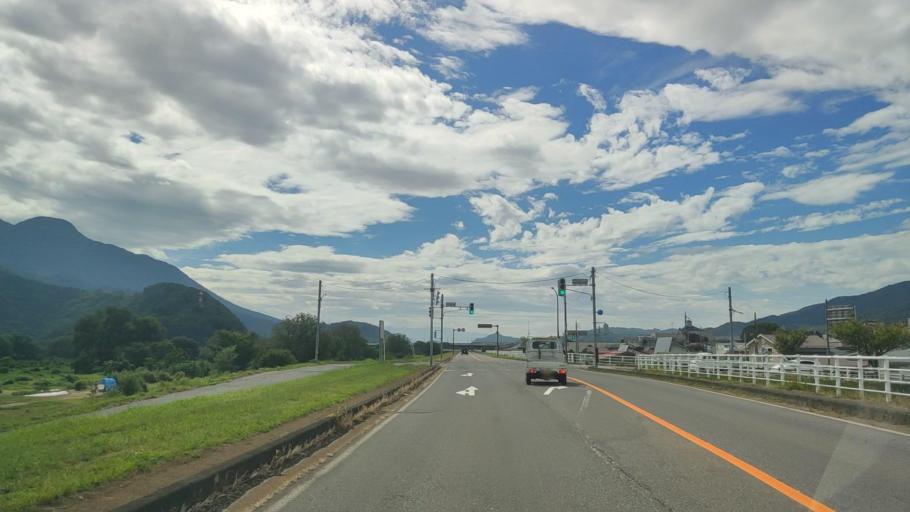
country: JP
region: Nagano
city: Iiyama
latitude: 36.8497
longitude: 138.3657
